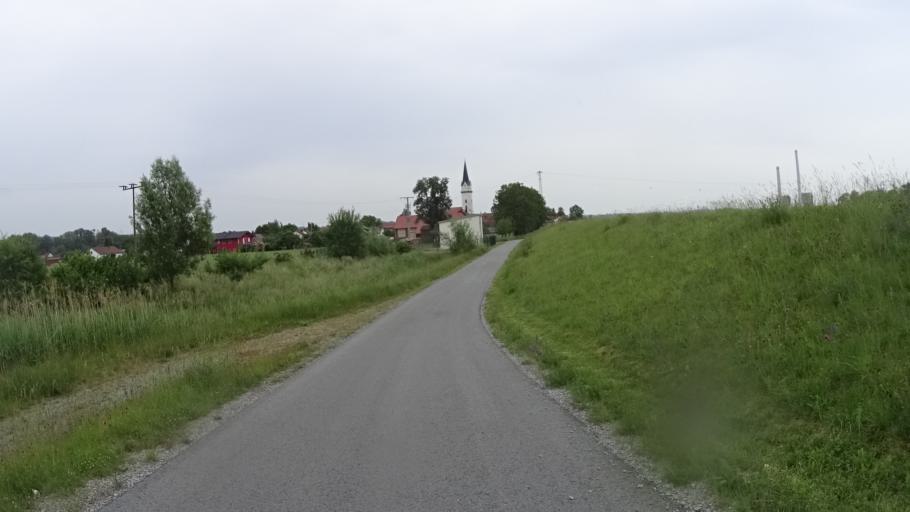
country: DE
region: Bavaria
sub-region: Lower Bavaria
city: Hofkirchen
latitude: 48.6823
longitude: 13.1150
